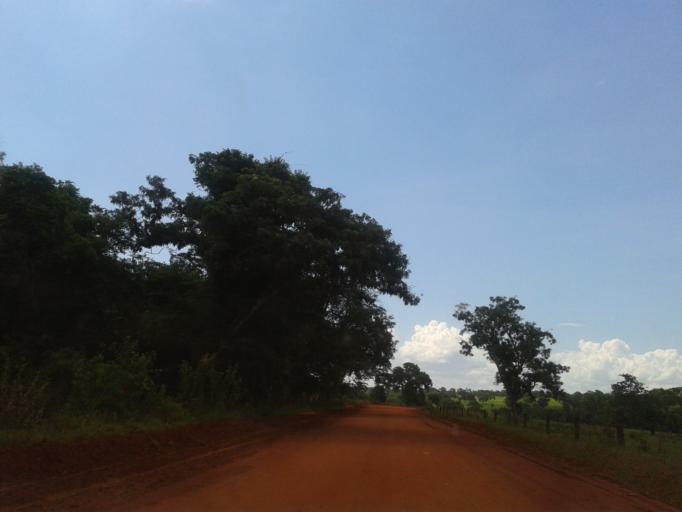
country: BR
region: Minas Gerais
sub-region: Santa Vitoria
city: Santa Vitoria
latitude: -19.1487
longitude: -50.3880
